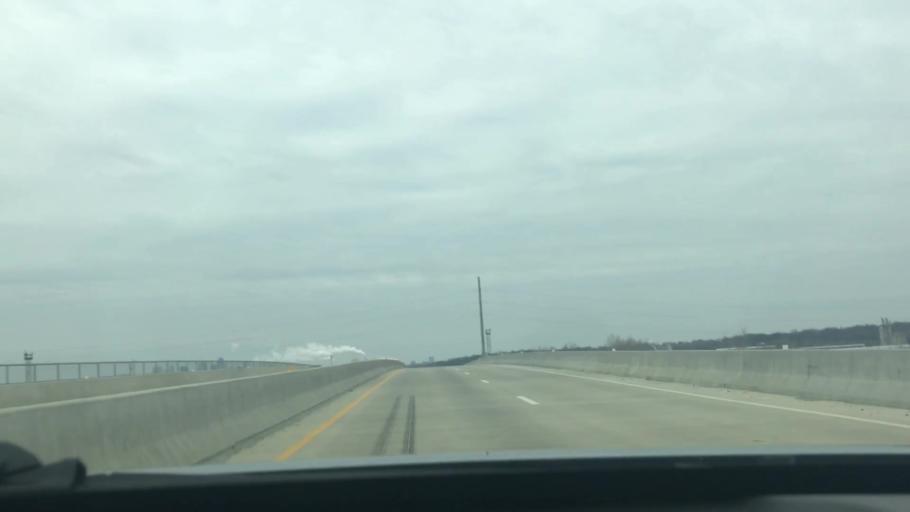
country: US
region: Missouri
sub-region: Platte County
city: Riverside
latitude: 39.1566
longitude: -94.6236
